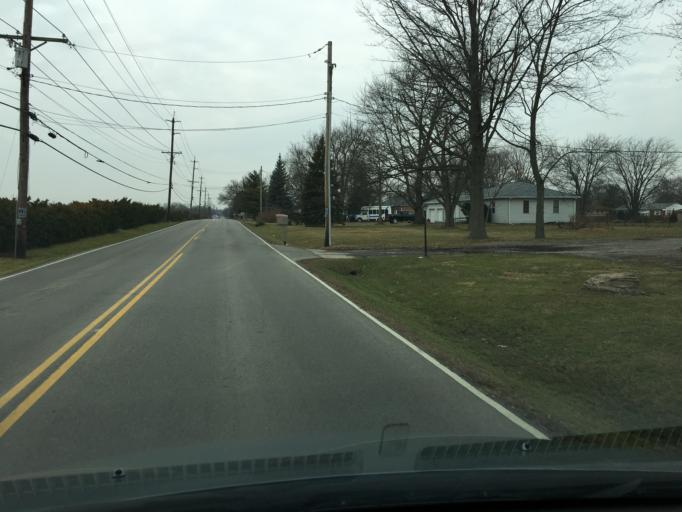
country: US
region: Ohio
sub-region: Hamilton County
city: Highpoint
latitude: 39.3189
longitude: -84.3360
